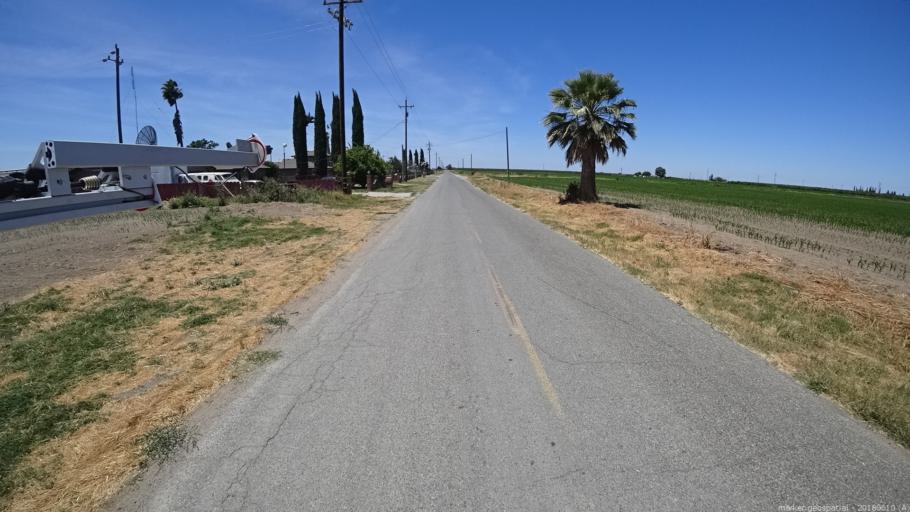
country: US
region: California
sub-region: Madera County
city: Chowchilla
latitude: 37.0544
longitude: -120.3410
